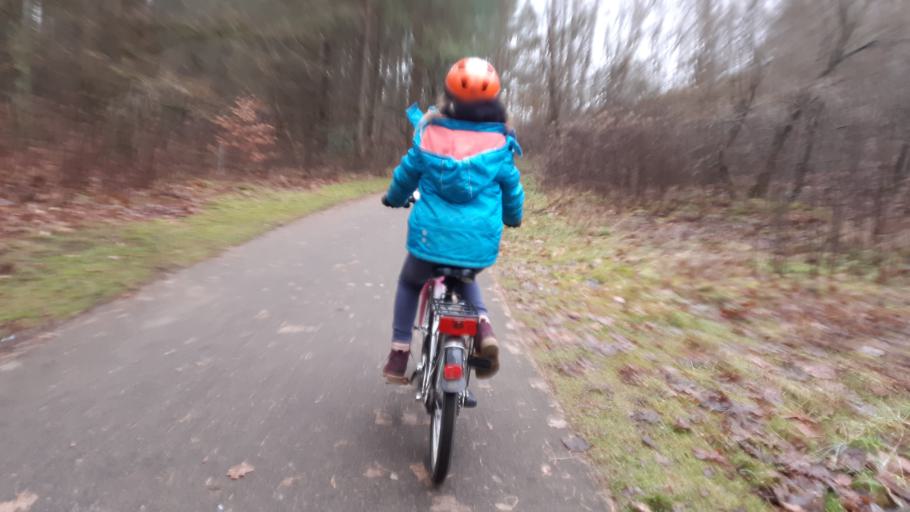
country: DE
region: Brandenburg
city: Templin
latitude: 53.1158
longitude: 13.5203
